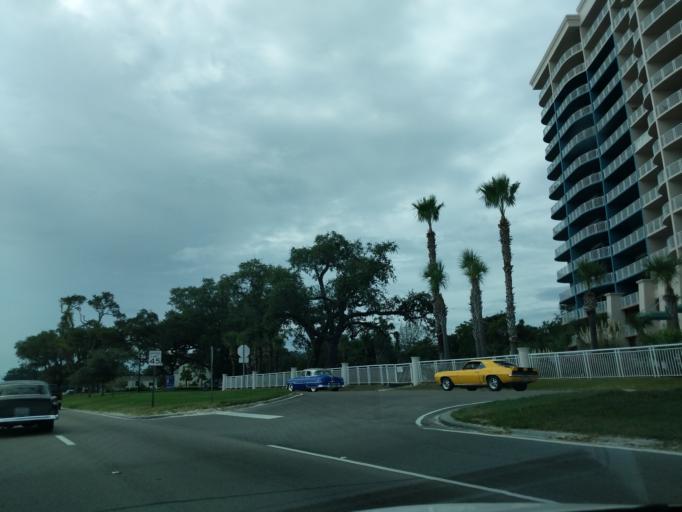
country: US
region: Mississippi
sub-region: Harrison County
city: Gulfport
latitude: 30.3876
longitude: -89.0040
